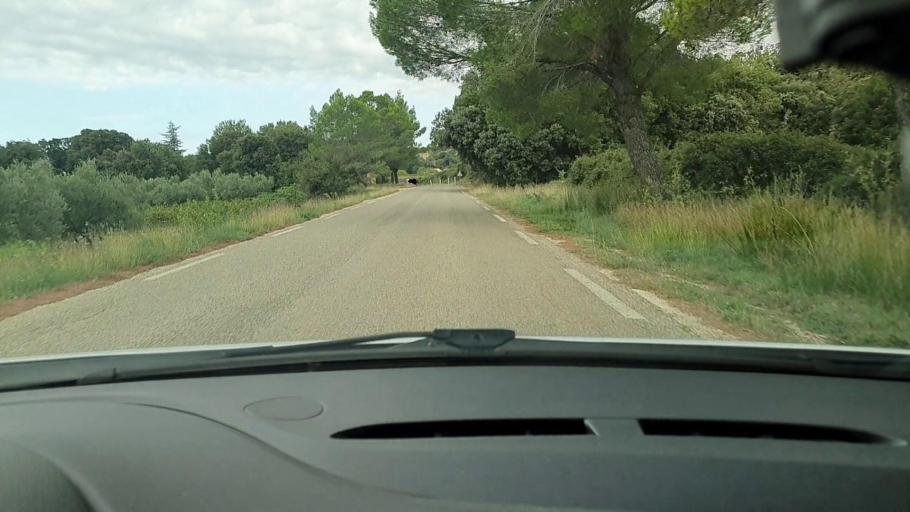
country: FR
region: Languedoc-Roussillon
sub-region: Departement du Gard
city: Montaren-et-Saint-Mediers
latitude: 44.0553
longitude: 4.3284
